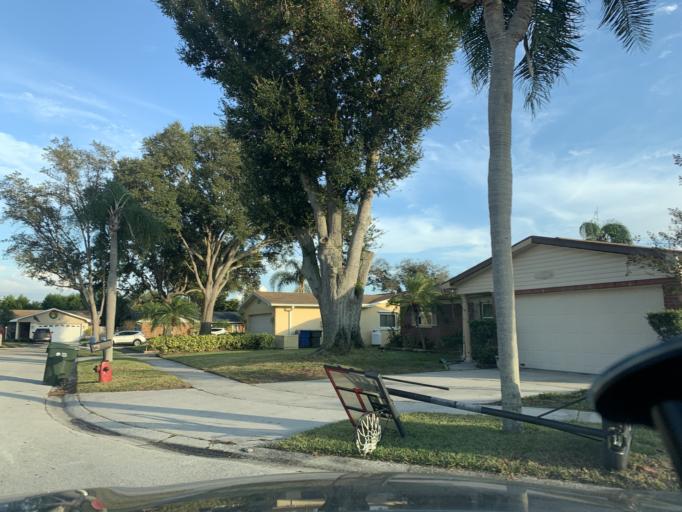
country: US
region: Florida
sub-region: Pinellas County
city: Ridgecrest
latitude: 27.8896
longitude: -82.7965
